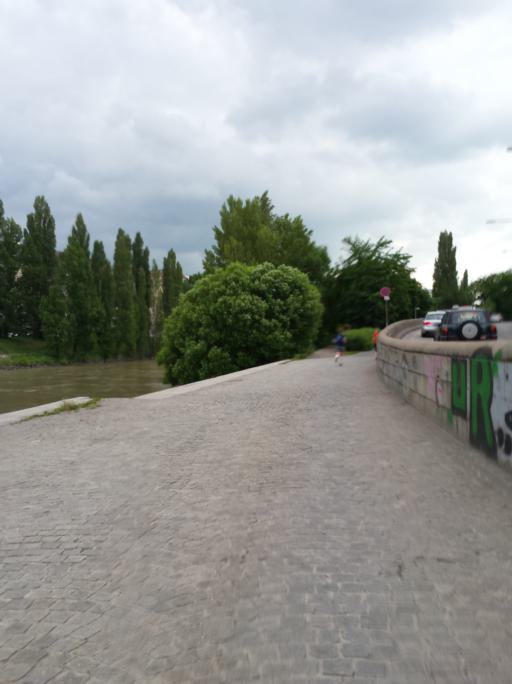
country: AT
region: Vienna
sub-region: Wien Stadt
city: Vienna
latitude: 48.2127
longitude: 16.3923
